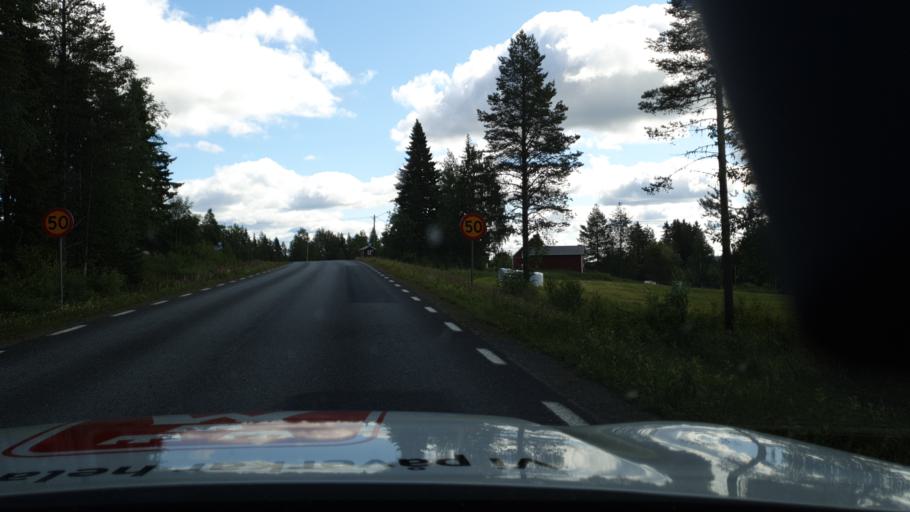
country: SE
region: Vaesterbotten
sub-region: Mala Kommun
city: Mala
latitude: 65.1498
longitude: 18.6380
